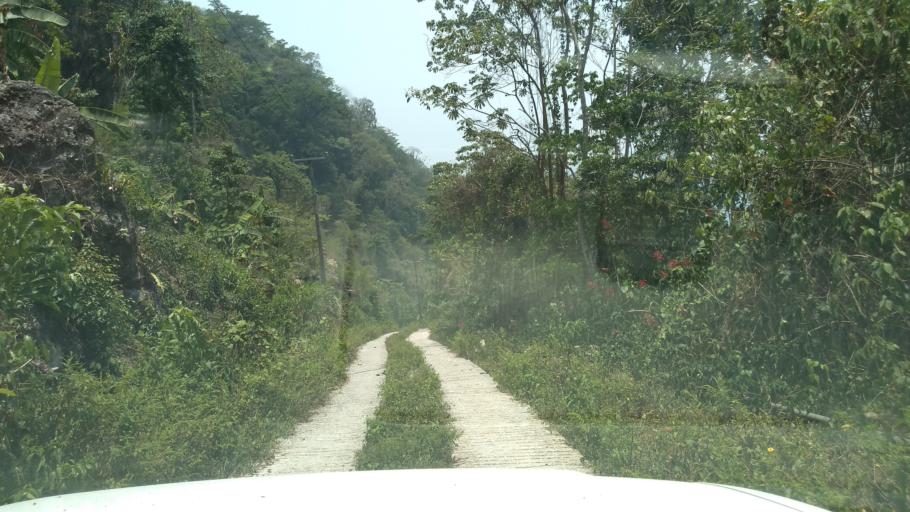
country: MX
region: Veracruz
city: Motzorongo
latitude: 18.5981
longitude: -96.7368
